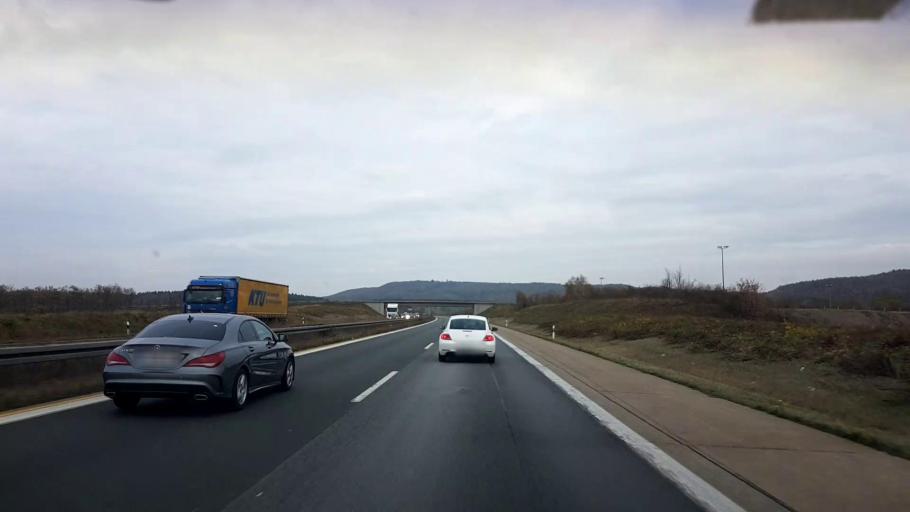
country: DE
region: Bavaria
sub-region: Regierungsbezirk Unterfranken
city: Castell
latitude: 49.7721
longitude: 10.3744
